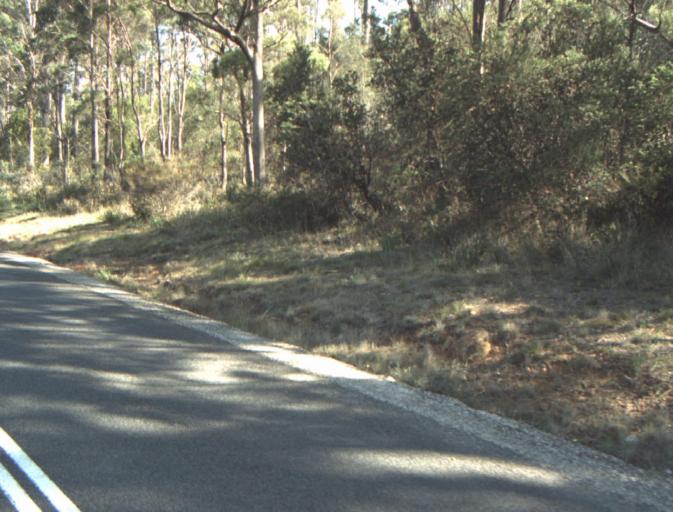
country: AU
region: Tasmania
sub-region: Launceston
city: Mayfield
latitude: -41.3328
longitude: 147.1792
